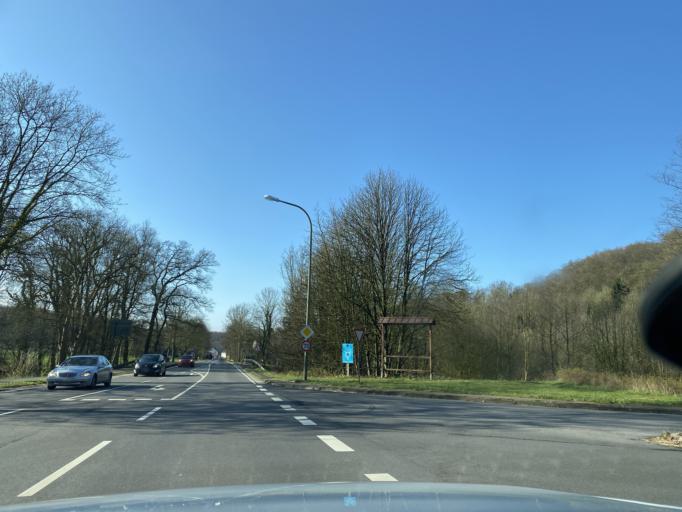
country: DE
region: North Rhine-Westphalia
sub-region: Regierungsbezirk Koln
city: Odenthal
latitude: 51.0387
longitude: 7.1204
